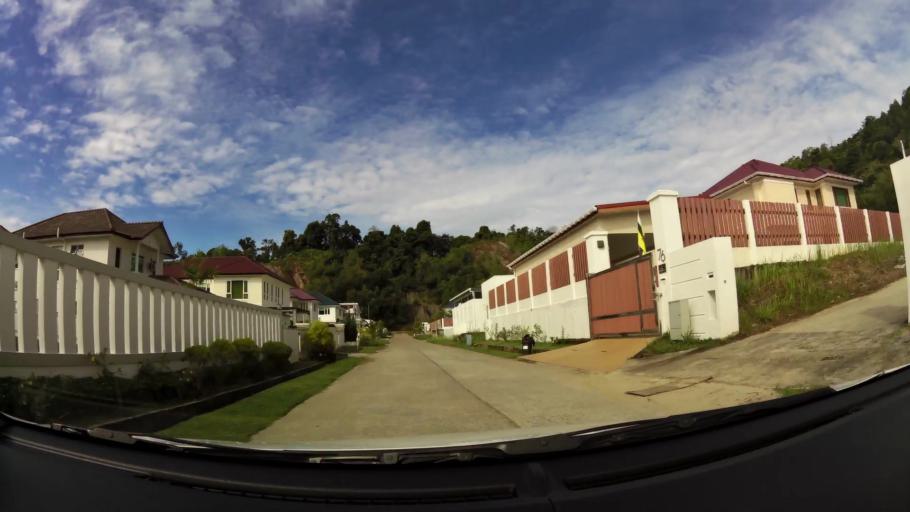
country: BN
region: Brunei and Muara
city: Bandar Seri Begawan
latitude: 4.8979
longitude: 114.9634
